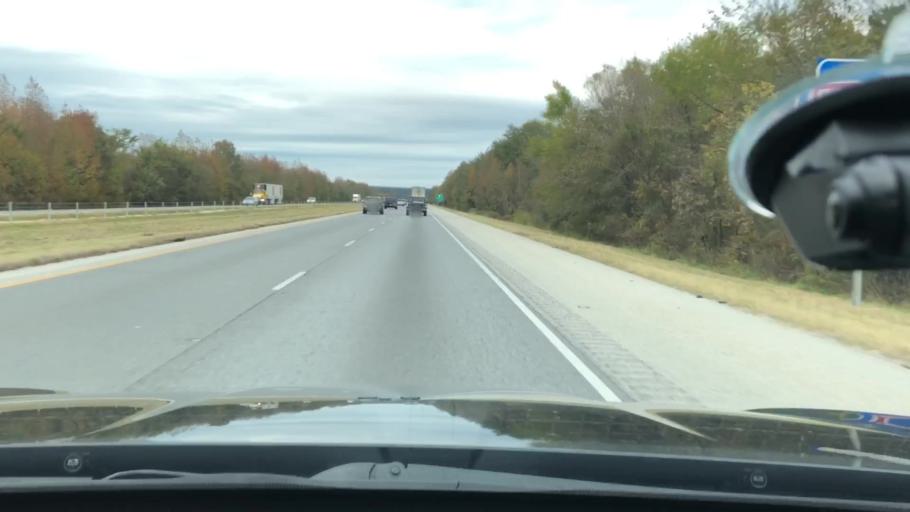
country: US
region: Arkansas
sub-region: Clark County
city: Arkadelphia
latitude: 34.1638
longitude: -93.0762
